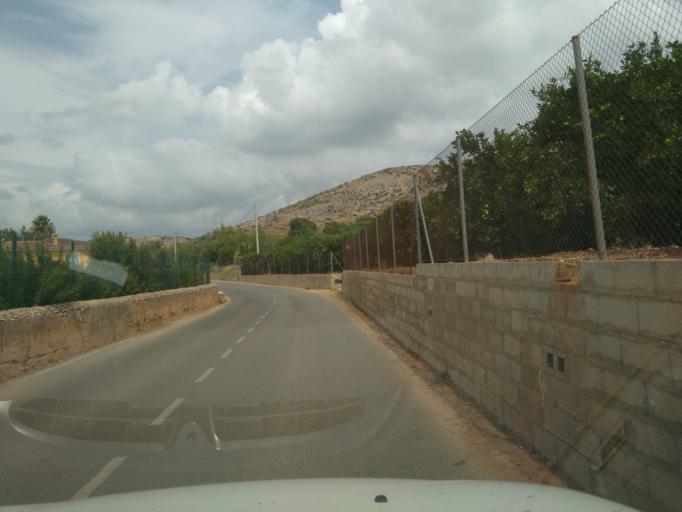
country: ES
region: Valencia
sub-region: Provincia de Valencia
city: La Pobla Llarga
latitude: 39.0833
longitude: -0.4237
